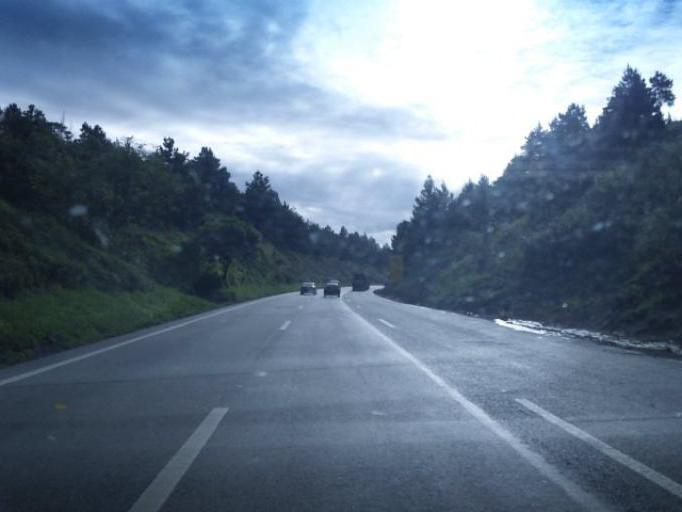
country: BR
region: Parana
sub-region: Campina Grande Do Sul
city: Campina Grande do Sul
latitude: -25.1041
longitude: -48.8367
